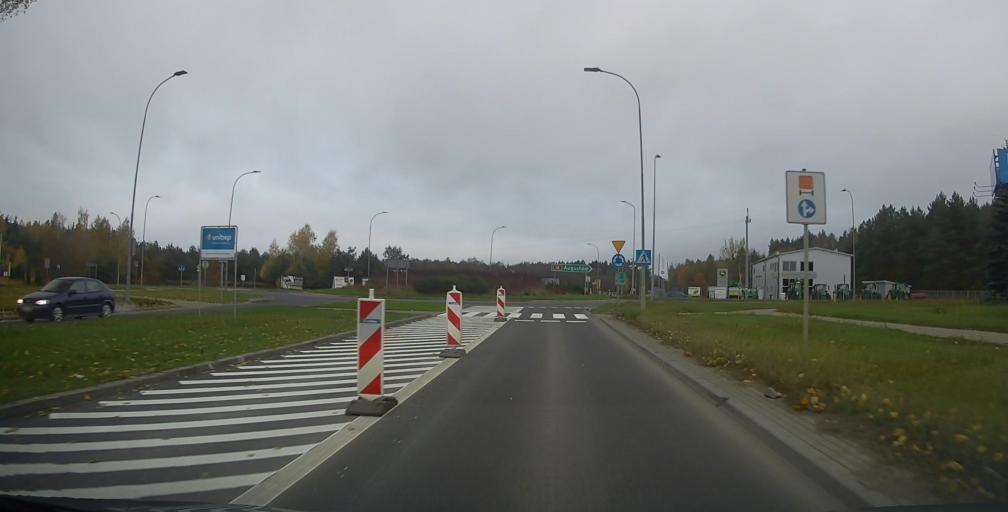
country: PL
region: Warmian-Masurian Voivodeship
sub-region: Powiat elcki
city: Elk
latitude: 53.8330
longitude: 22.3895
